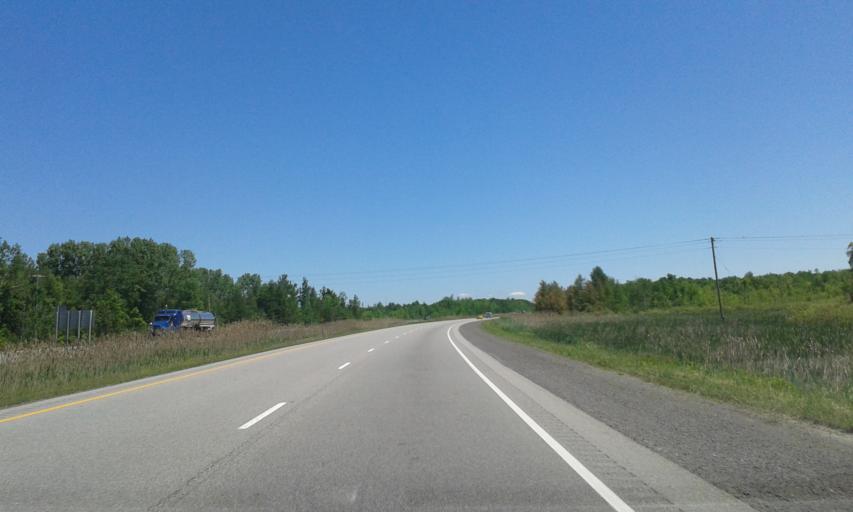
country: CA
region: Ontario
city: Prescott
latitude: 44.7776
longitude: -75.4571
